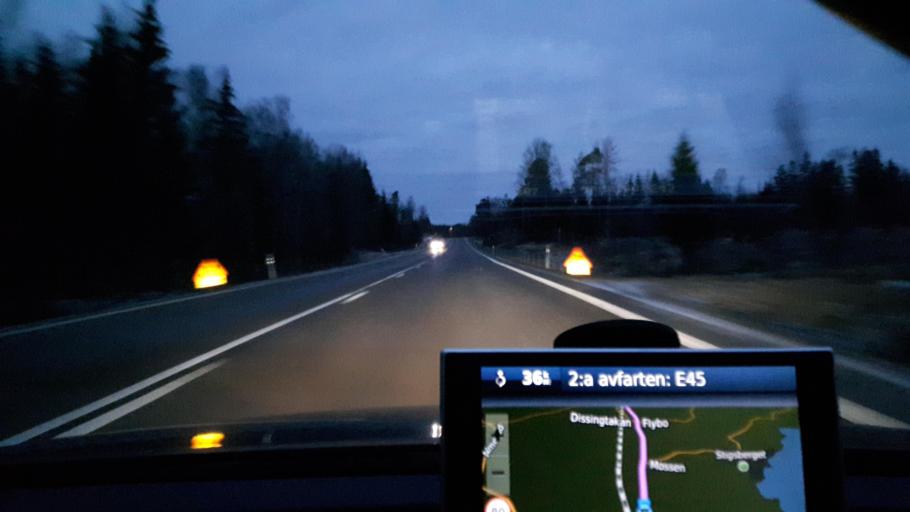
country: SE
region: Vaestra Goetaland
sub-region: Vanersborgs Kommun
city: Vanersborg
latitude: 58.4122
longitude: 12.2932
